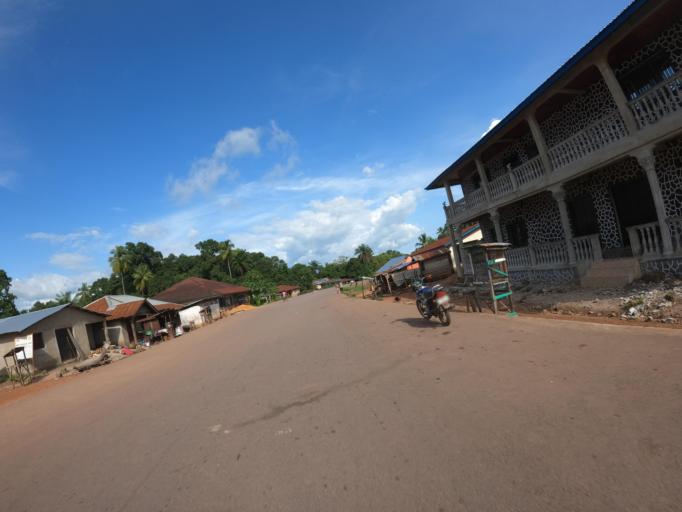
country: SL
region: Northern Province
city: Makeni
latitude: 9.0331
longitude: -12.1601
